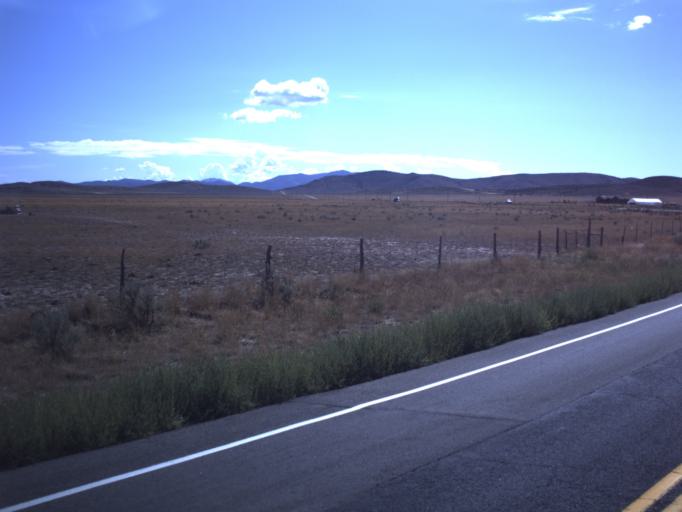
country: US
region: Utah
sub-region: Tooele County
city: Tooele
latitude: 40.0885
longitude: -112.4303
